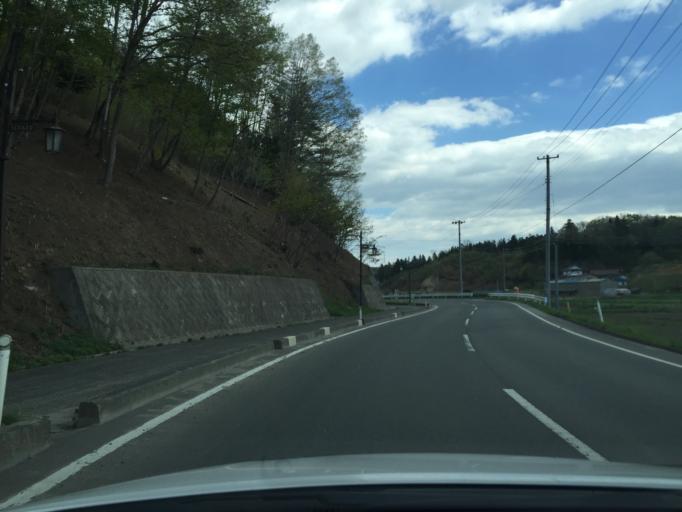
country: JP
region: Fukushima
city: Yanagawamachi-saiwaicho
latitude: 37.6905
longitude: 140.7435
